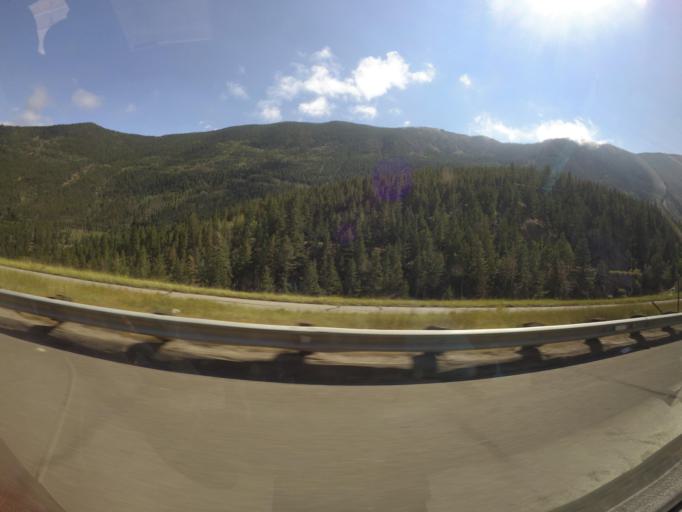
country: US
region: Colorado
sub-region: Clear Creek County
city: Georgetown
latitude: 39.6985
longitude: -105.7249
